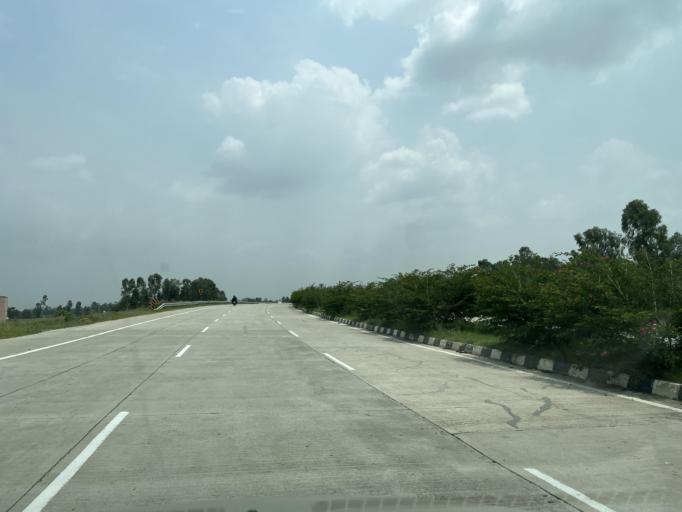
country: IN
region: Uttar Pradesh
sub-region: Bijnor
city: Nagina
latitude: 29.4305
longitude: 78.4145
